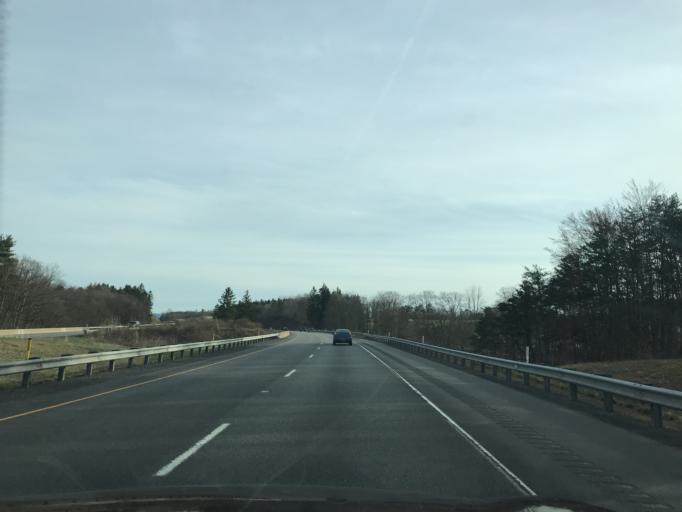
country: US
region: Pennsylvania
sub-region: Lycoming County
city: Muncy
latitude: 41.1481
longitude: -76.8021
